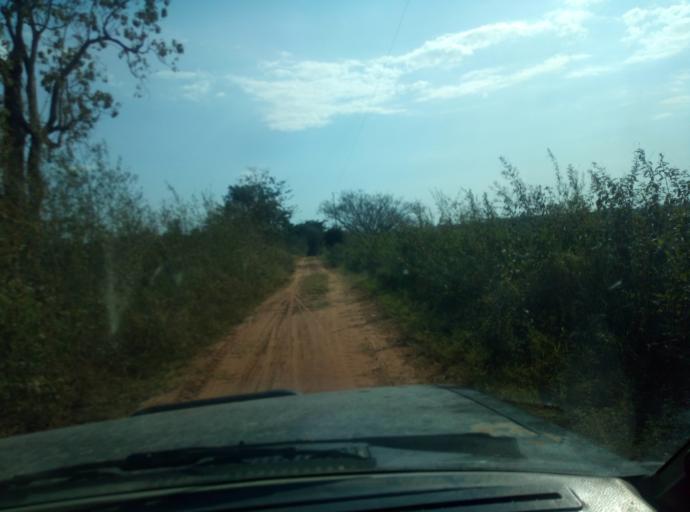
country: PY
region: Caaguazu
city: Doctor Cecilio Baez
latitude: -25.1426
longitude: -56.2525
